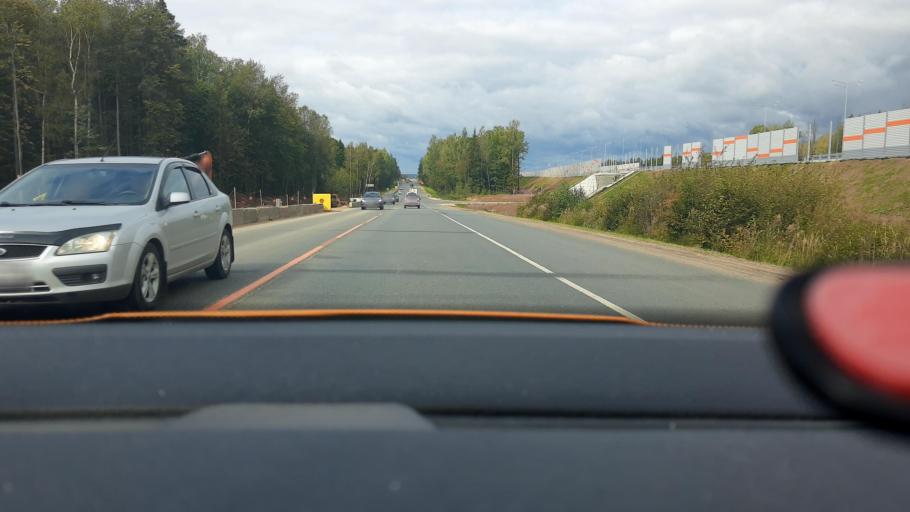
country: RU
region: Moskovskaya
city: Zelenogradskiy
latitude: 56.0977
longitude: 37.9759
